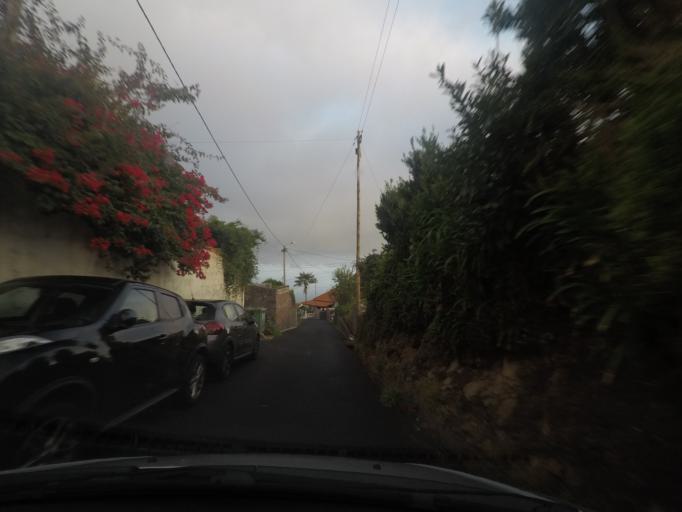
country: PT
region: Madeira
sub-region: Santa Cruz
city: Camacha
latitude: 32.6819
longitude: -16.8533
